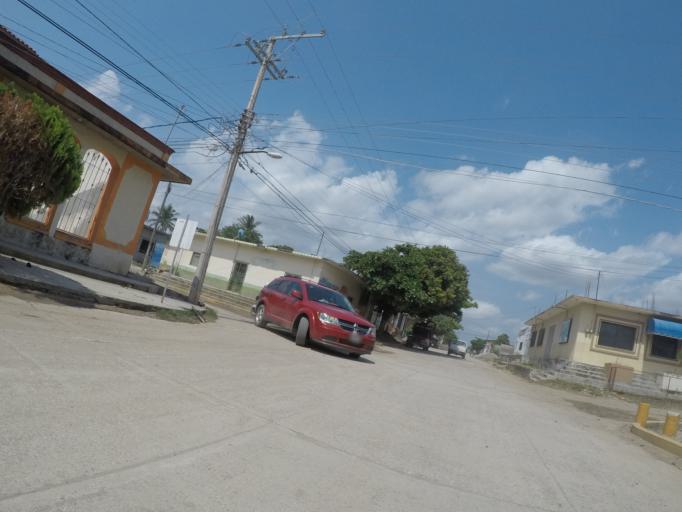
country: MX
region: Oaxaca
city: Union Hidalgo
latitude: 16.4681
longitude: -94.8305
